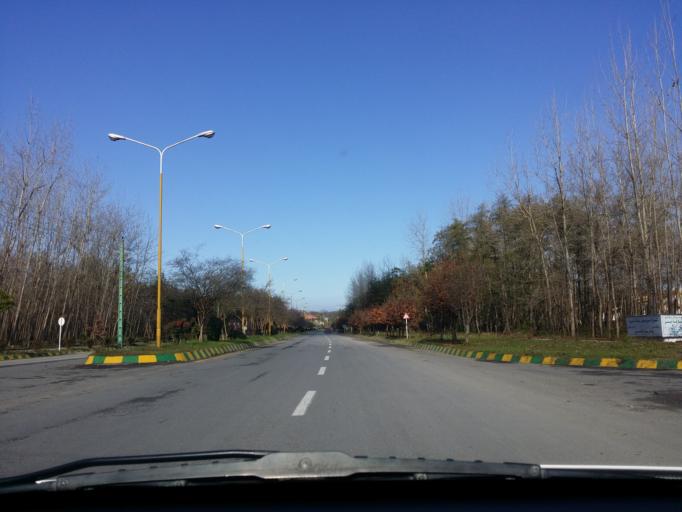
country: IR
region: Mazandaran
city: Chalus
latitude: 36.6784
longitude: 51.3064
